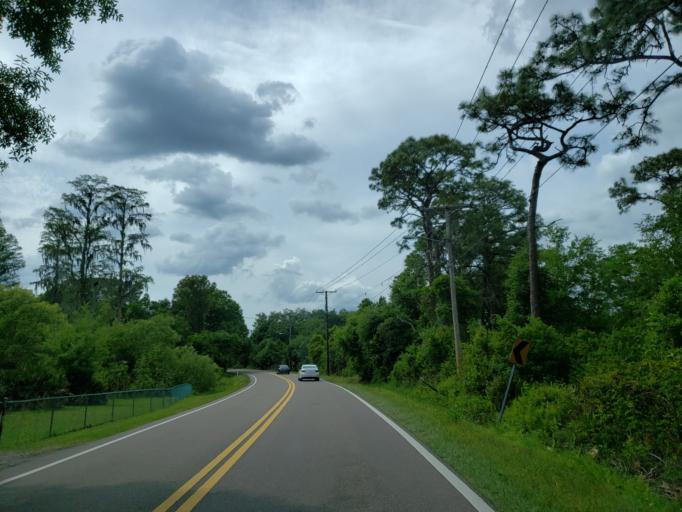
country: US
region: Florida
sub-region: Hillsborough County
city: Keystone
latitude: 28.1308
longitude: -82.6177
